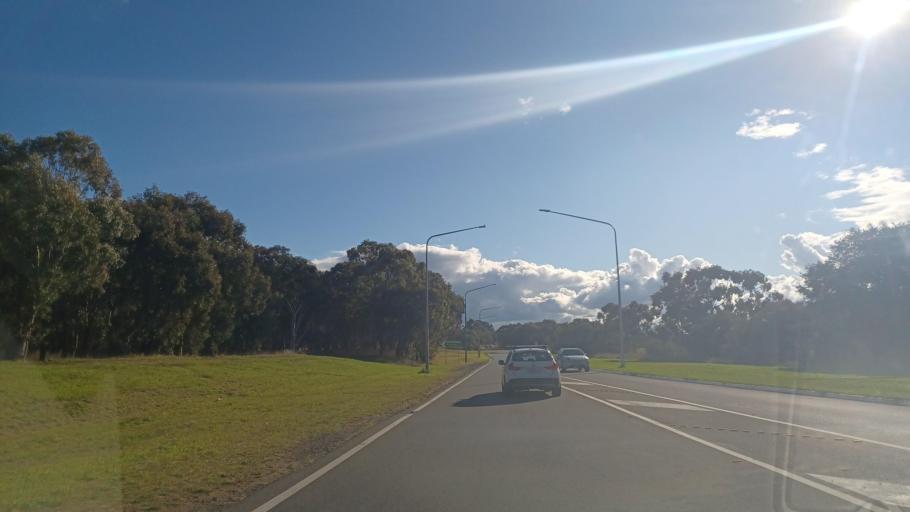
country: AU
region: Australian Capital Territory
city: Belconnen
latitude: -35.1925
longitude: 149.0656
